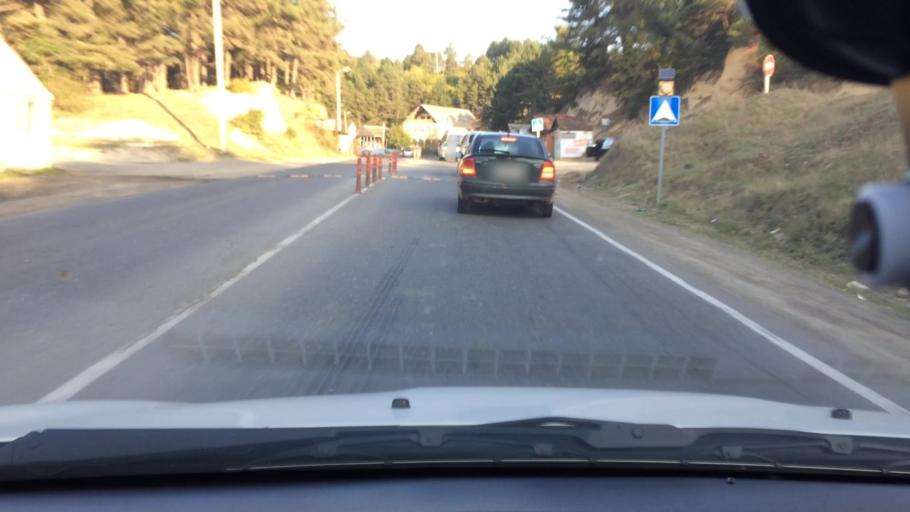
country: GE
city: Surami
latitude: 42.0268
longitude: 43.5609
